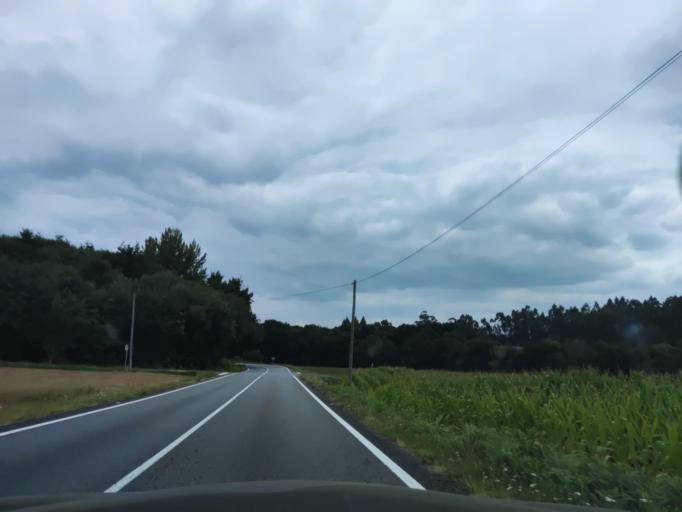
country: ES
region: Galicia
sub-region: Provincia da Coruna
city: Teo
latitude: 42.7620
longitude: -8.5567
